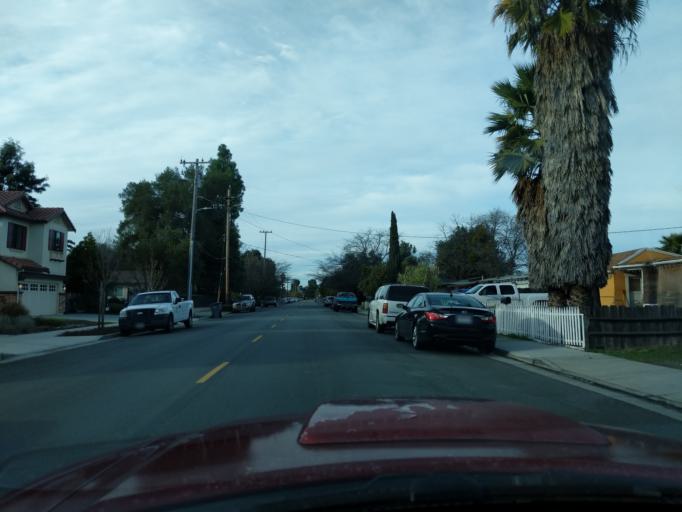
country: US
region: California
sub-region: Santa Clara County
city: Morgan Hill
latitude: 37.1142
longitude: -121.6411
